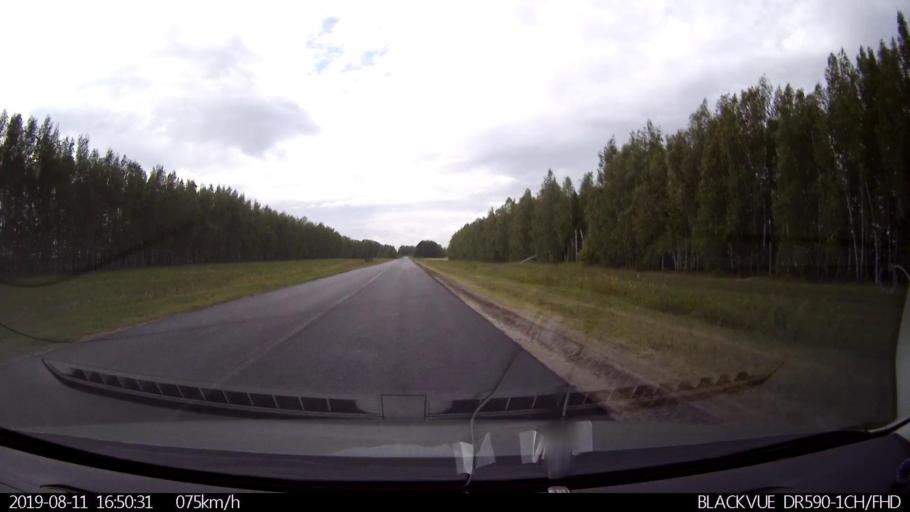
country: RU
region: Ulyanovsk
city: Mayna
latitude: 54.2294
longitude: 47.6865
